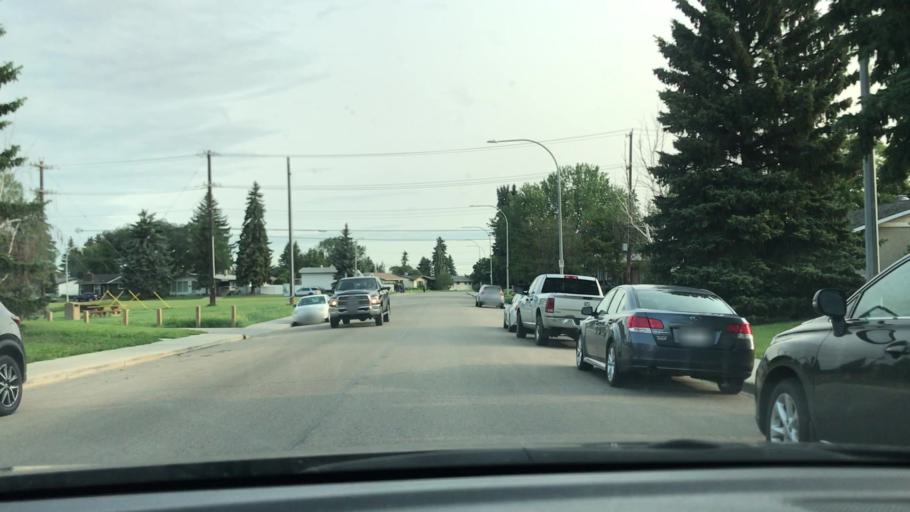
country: CA
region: Alberta
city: Edmonton
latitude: 53.5420
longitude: -113.4293
